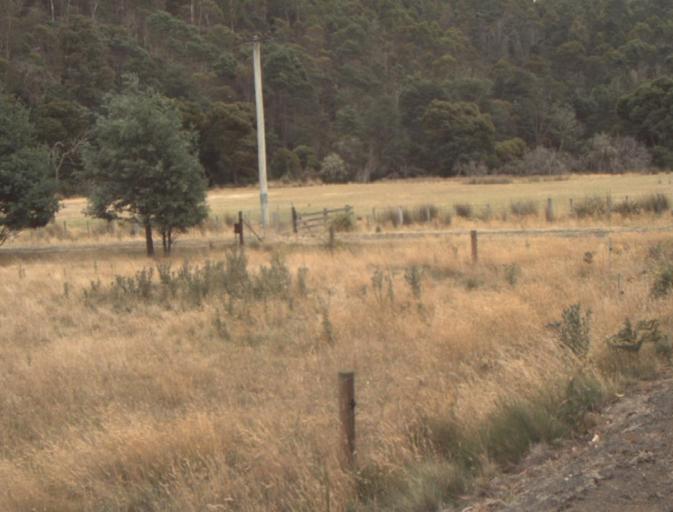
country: AU
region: Tasmania
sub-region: Northern Midlands
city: Evandale
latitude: -41.4666
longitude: 147.4943
